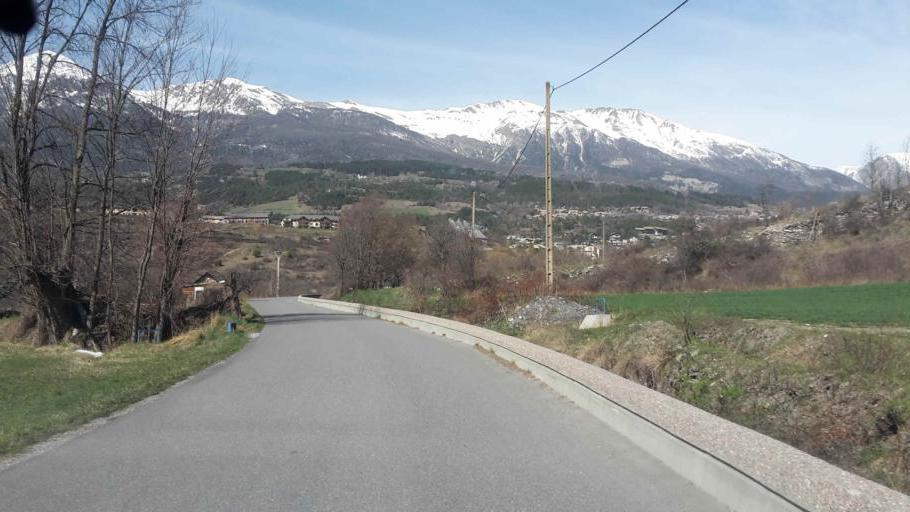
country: FR
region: Provence-Alpes-Cote d'Azur
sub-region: Departement des Hautes-Alpes
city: Embrun
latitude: 44.5615
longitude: 6.5093
